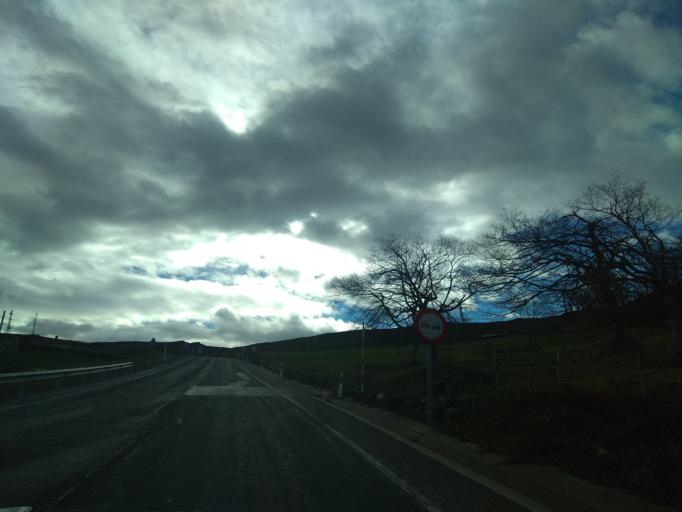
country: ES
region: Castille and Leon
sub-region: Provincia de Burgos
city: Arija
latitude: 43.0576
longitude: -3.8869
